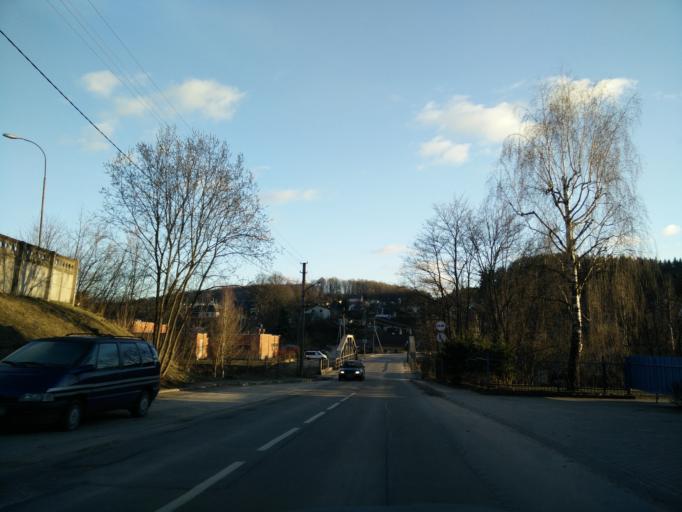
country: LT
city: Skaidiskes
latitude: 54.6926
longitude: 25.3973
